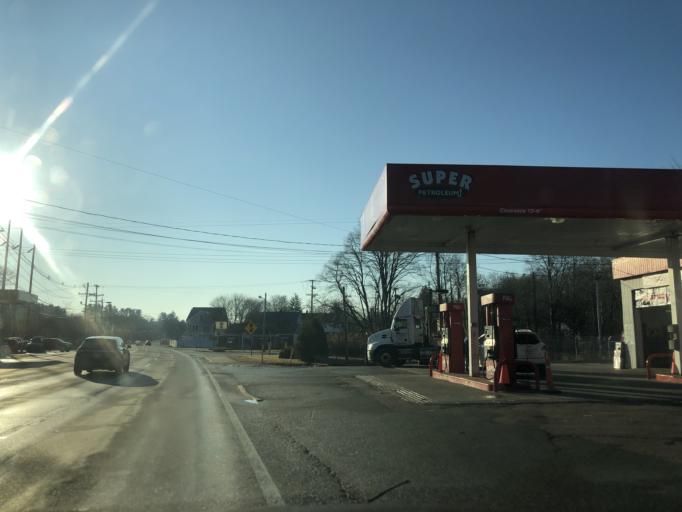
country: US
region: Massachusetts
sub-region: Norfolk County
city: Avon
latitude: 42.1233
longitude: -71.0346
